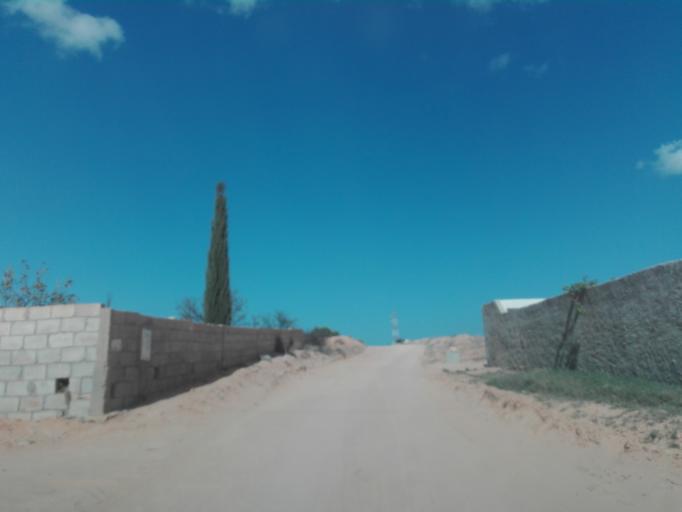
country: TN
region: Madanin
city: Bin Qirdan
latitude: 33.1637
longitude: 11.1957
